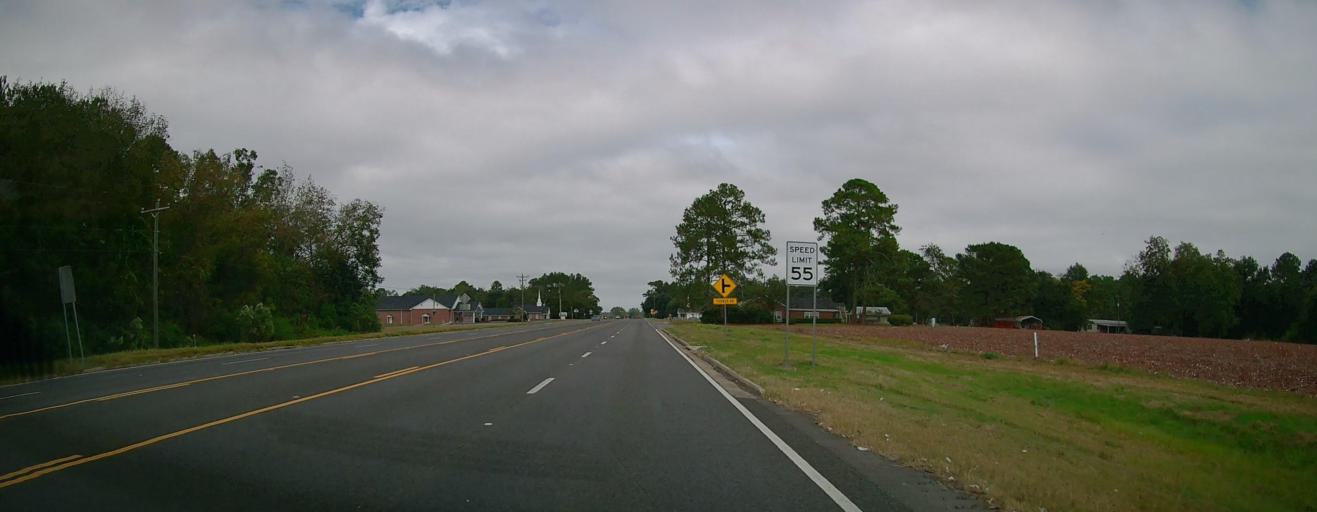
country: US
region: Georgia
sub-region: Colquitt County
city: Moultrie
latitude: 31.0678
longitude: -83.8256
